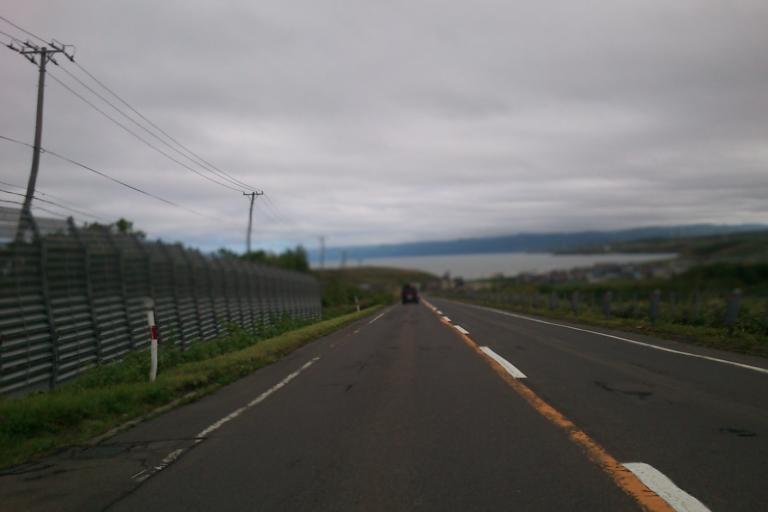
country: JP
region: Hokkaido
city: Ishikari
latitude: 43.3064
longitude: 141.4120
